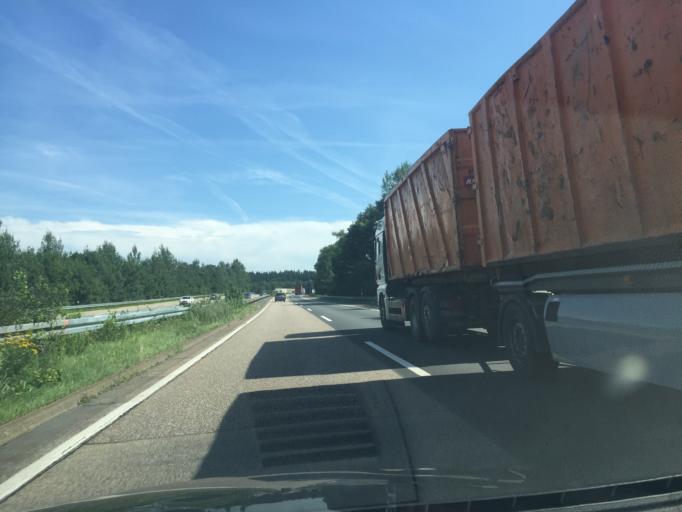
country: DE
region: North Rhine-Westphalia
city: Meinerzhagen
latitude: 51.0821
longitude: 7.6921
